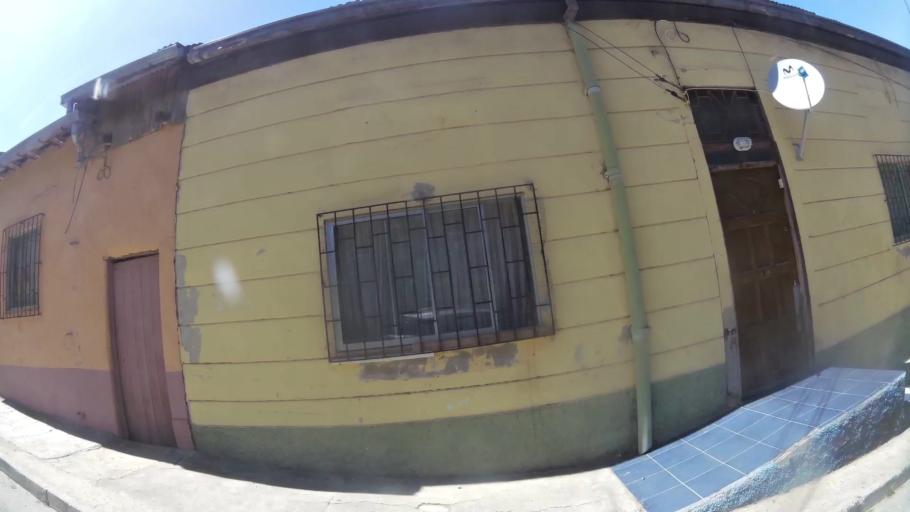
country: CL
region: Valparaiso
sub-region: Provincia de Valparaiso
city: Valparaiso
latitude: -33.0487
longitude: -71.5980
